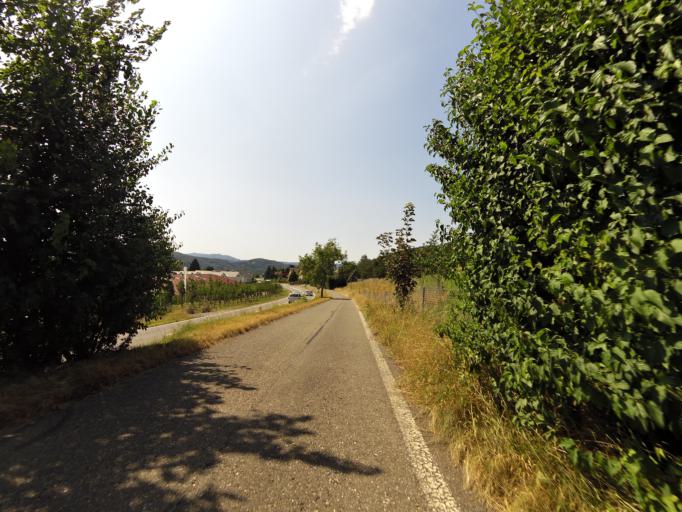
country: CH
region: Aargau
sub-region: Bezirk Baden
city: Birmenstorf
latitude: 47.4569
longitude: 8.2656
